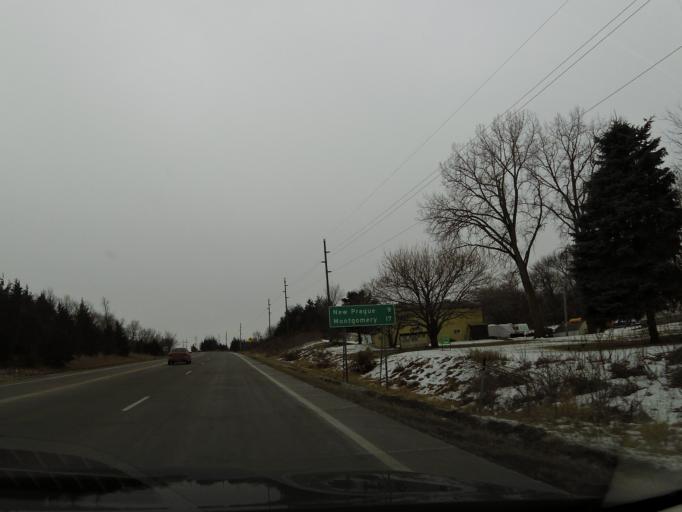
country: US
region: Minnesota
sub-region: Scott County
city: Jordan
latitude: 44.6539
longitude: -93.6285
